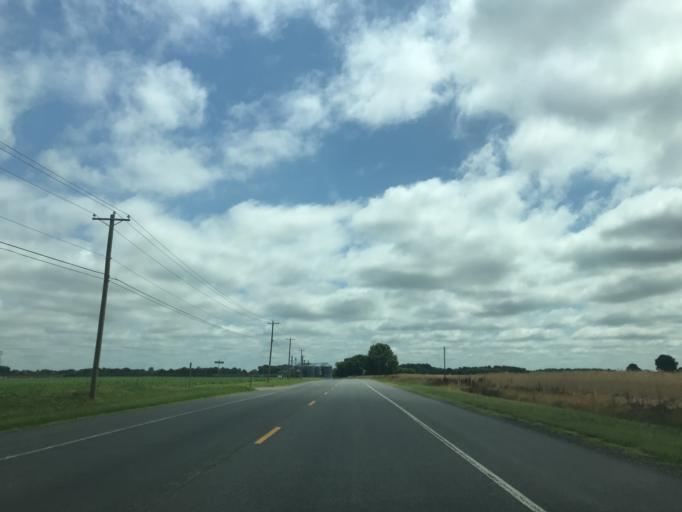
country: US
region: Maryland
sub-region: Caroline County
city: Ridgely
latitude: 38.9333
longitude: -75.9000
